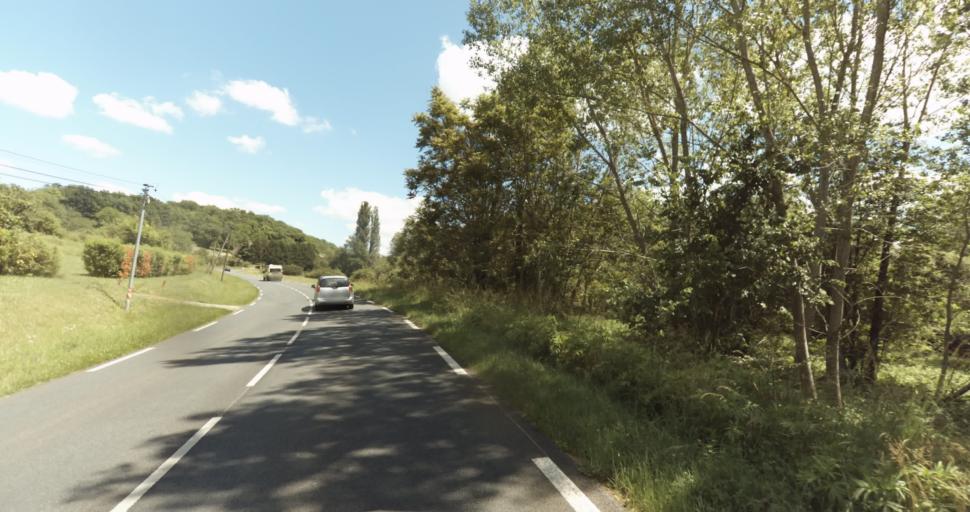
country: FR
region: Aquitaine
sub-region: Departement de la Dordogne
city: Le Bugue
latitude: 44.8410
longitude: 0.8542
